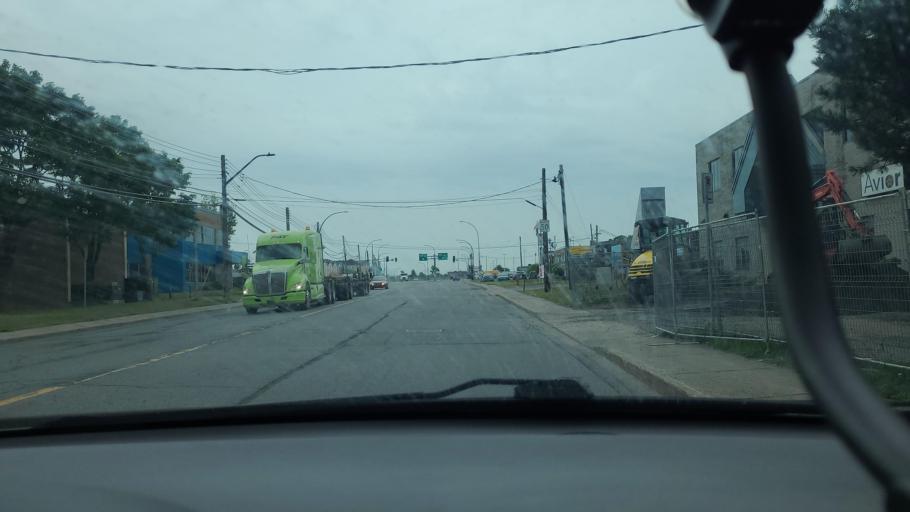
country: CA
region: Quebec
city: Cote-Saint-Luc
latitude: 45.4796
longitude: -73.7073
